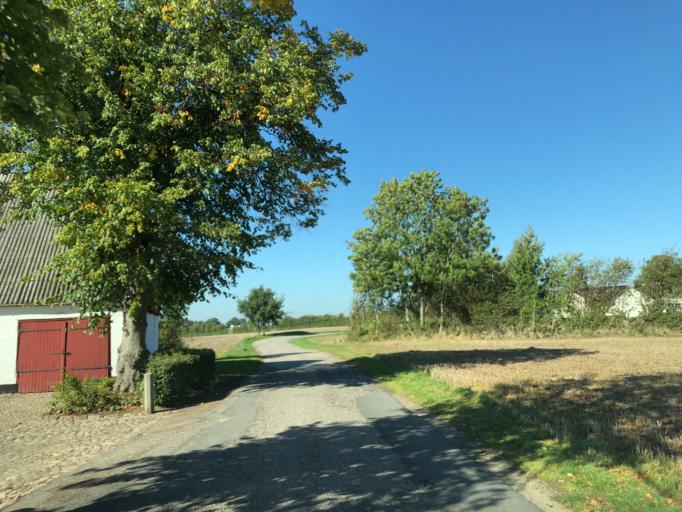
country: DK
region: South Denmark
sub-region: Sonderborg Kommune
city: Dybbol
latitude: 54.9460
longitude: 9.7307
